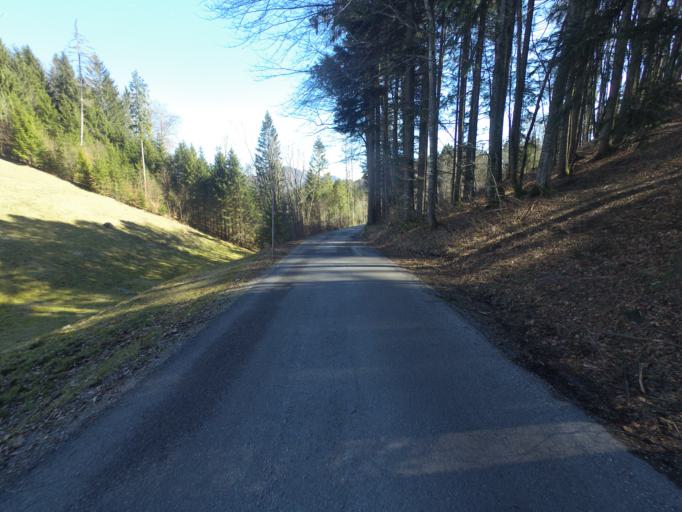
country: AT
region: Salzburg
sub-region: Politischer Bezirk Salzburg-Umgebung
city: Koppl
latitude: 47.8005
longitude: 13.1491
